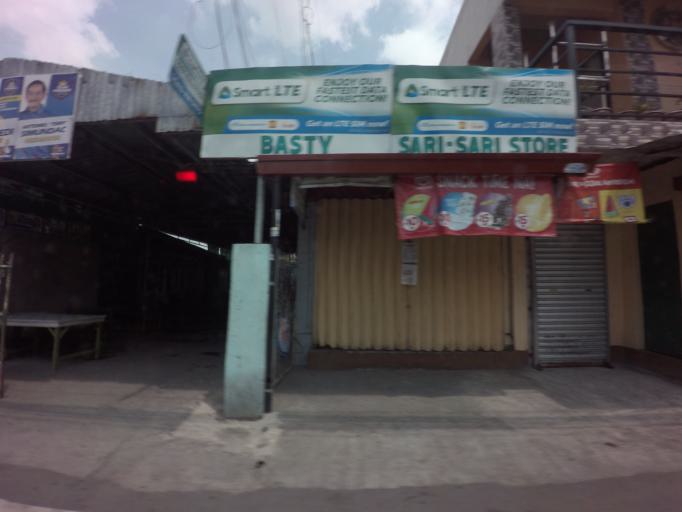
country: PH
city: Sambayanihan People's Village
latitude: 14.4592
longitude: 121.0537
